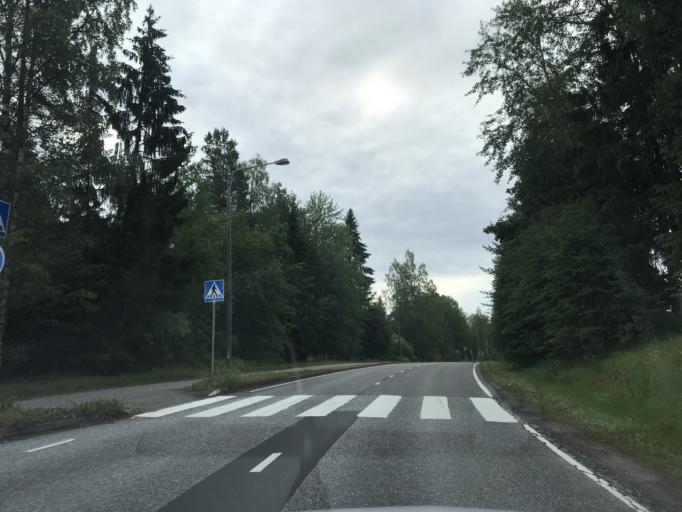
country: FI
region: Uusimaa
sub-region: Helsinki
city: Nurmijaervi
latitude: 60.3839
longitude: 24.6857
